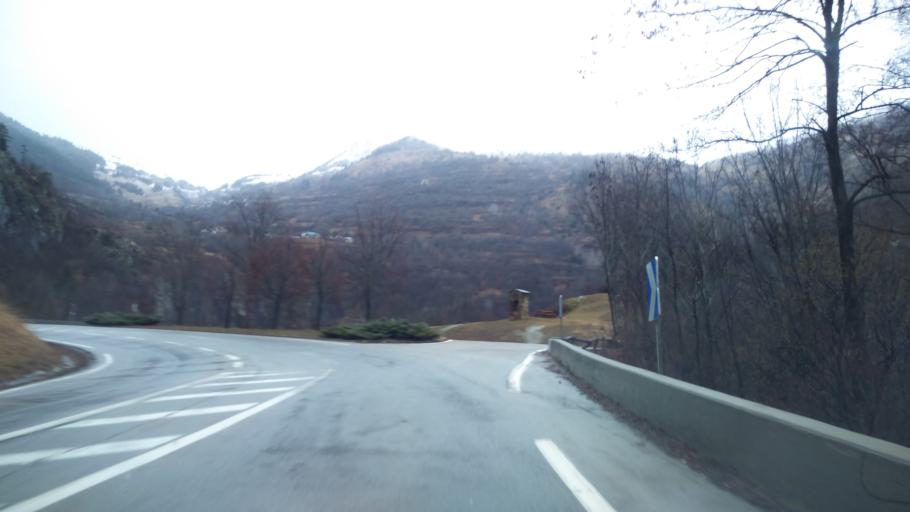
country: FR
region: Rhone-Alpes
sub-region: Departement de l'Isere
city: Mont-de-Lans
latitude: 45.0386
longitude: 6.1030
